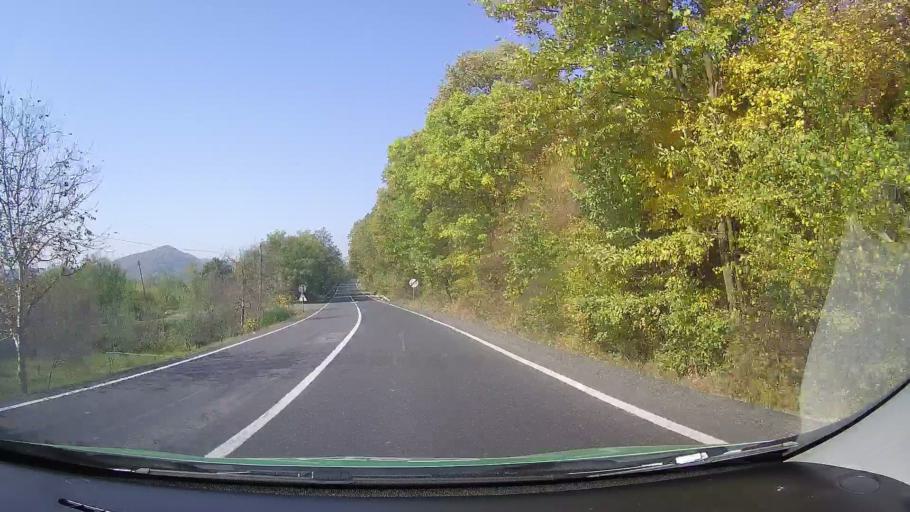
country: RO
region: Hunedoara
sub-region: Comuna Burjuc
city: Burjuc
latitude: 45.9405
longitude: 22.5248
